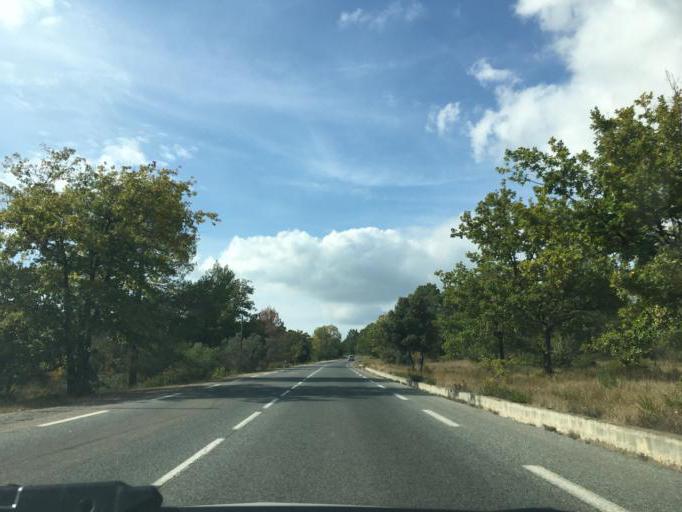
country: FR
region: Provence-Alpes-Cote d'Azur
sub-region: Departement du Var
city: Flayosc
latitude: 43.5437
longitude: 6.3471
